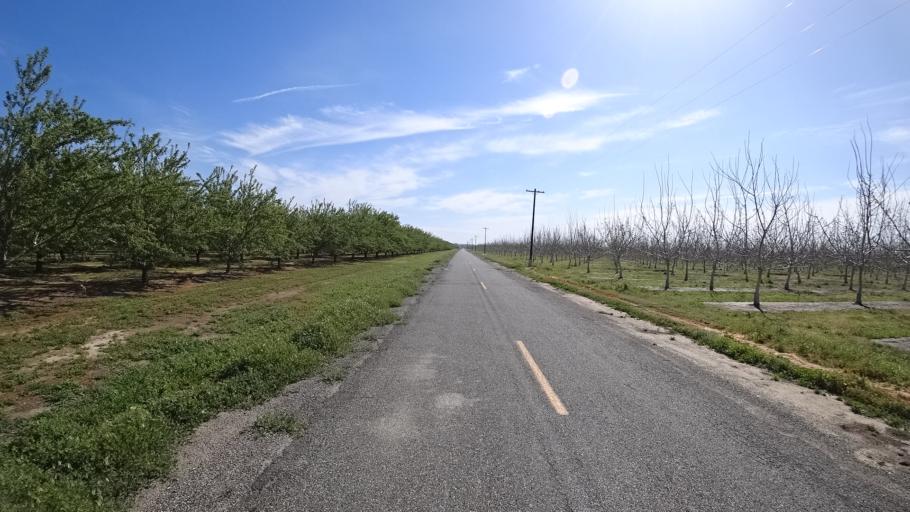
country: US
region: California
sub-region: Glenn County
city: Hamilton City
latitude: 39.6161
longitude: -122.0225
